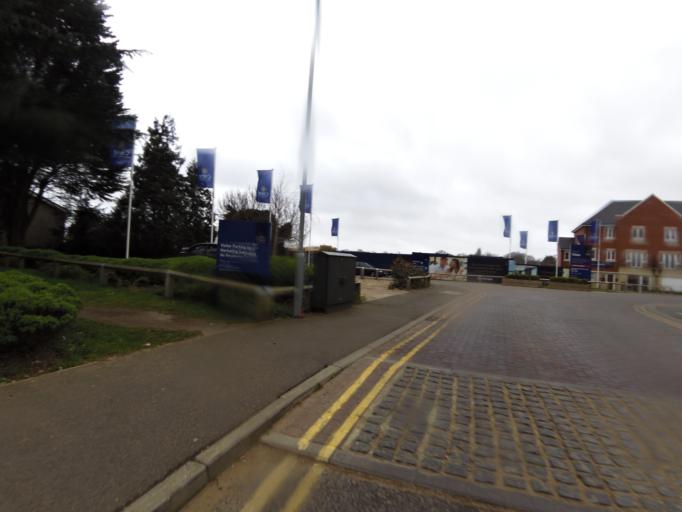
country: GB
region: England
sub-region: Suffolk
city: Ipswich
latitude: 52.0615
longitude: 1.1696
